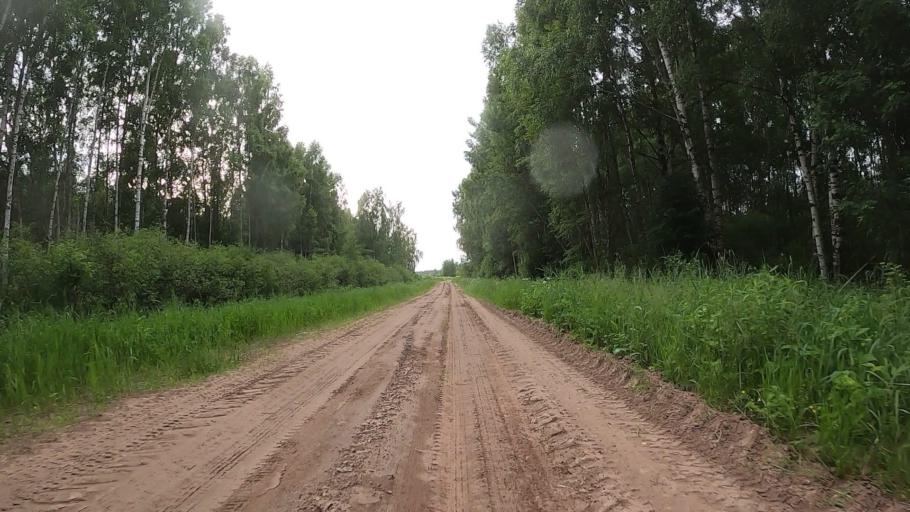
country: LV
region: Olaine
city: Olaine
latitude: 56.8223
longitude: 23.9711
